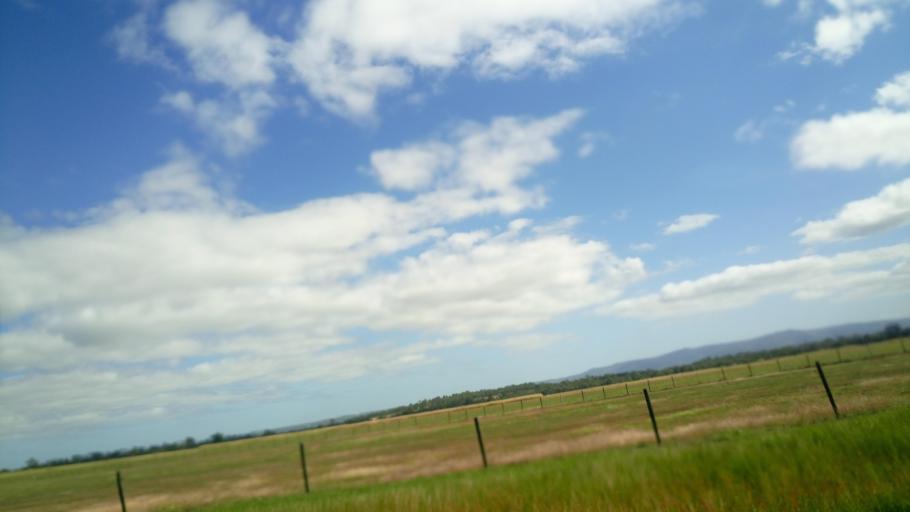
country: AU
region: Queensland
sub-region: Tablelands
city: Mareeba
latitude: -16.9691
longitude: 145.4567
